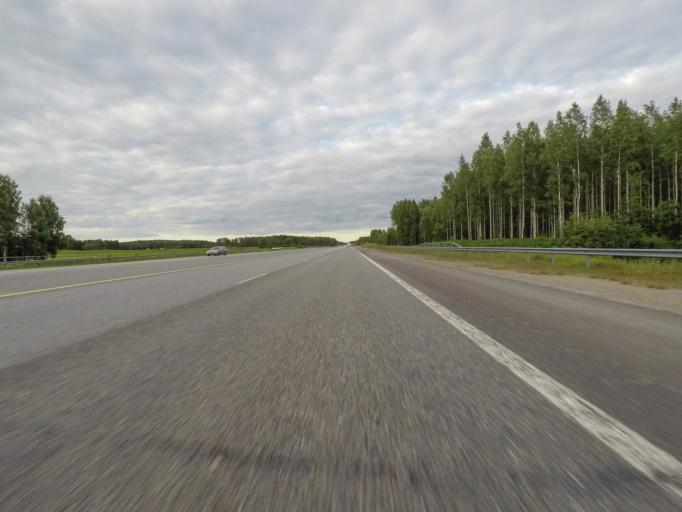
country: FI
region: Paijanne Tavastia
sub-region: Lahti
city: Heinola
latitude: 61.3090
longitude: 26.1086
